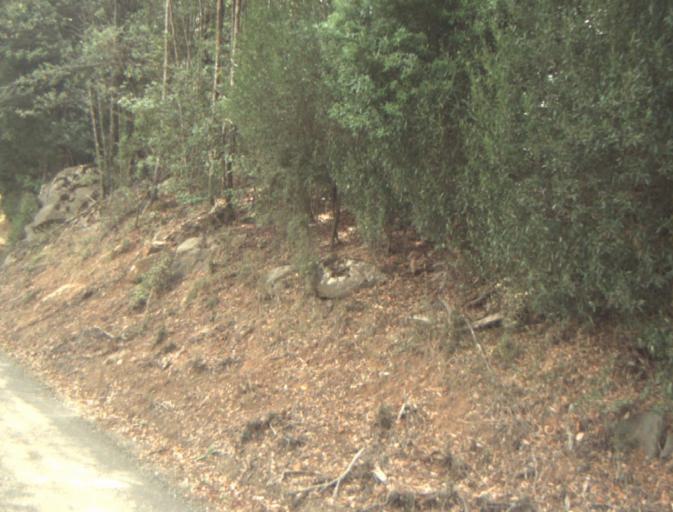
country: AU
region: Tasmania
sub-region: Launceston
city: Mayfield
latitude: -41.2777
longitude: 147.1902
